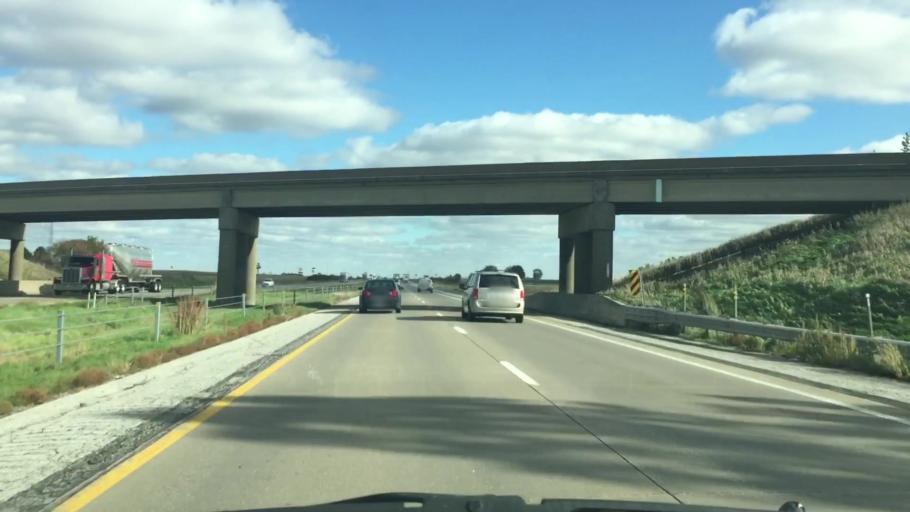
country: US
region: Iowa
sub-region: Scott County
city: Walcott
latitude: 41.6249
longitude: -90.8139
